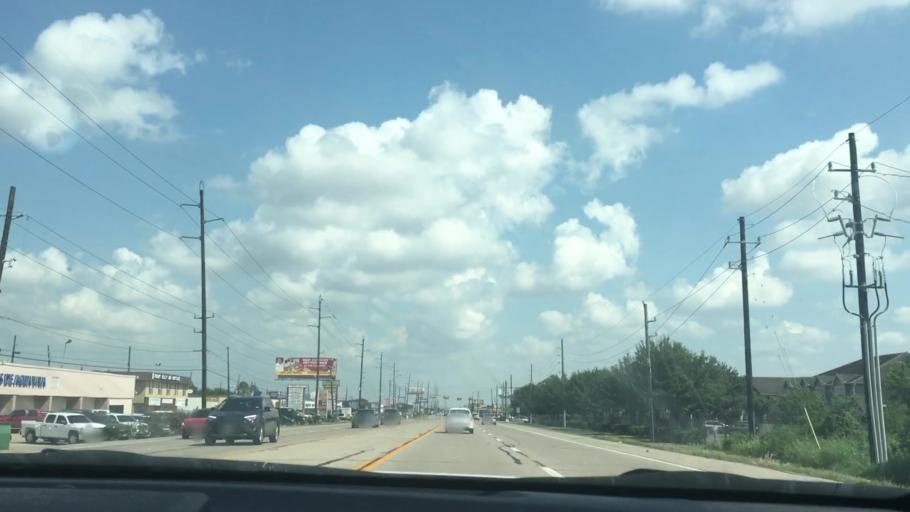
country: US
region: Texas
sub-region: Fort Bend County
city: Stafford
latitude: 29.6060
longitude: -95.5644
